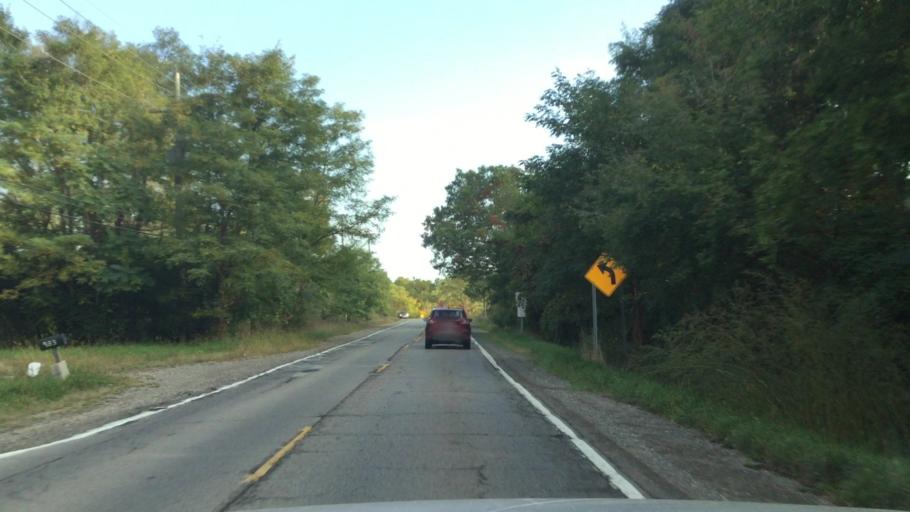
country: US
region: Michigan
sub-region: Oakland County
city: Wolverine Lake
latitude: 42.6243
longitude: -83.4557
